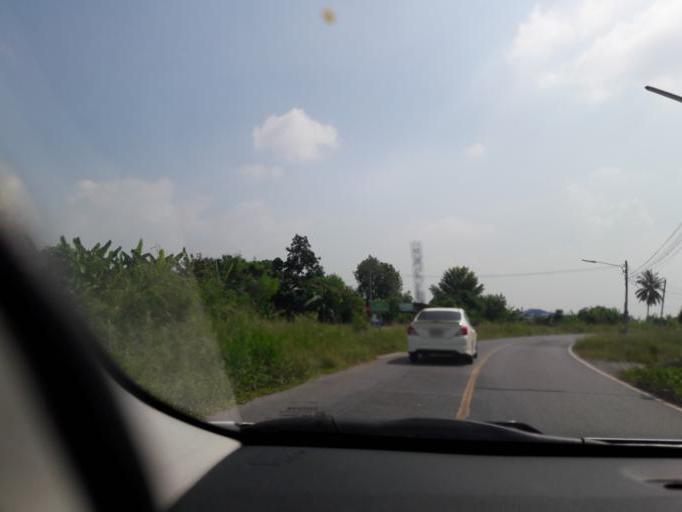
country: TH
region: Ang Thong
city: Ang Thong
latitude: 14.5979
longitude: 100.4027
